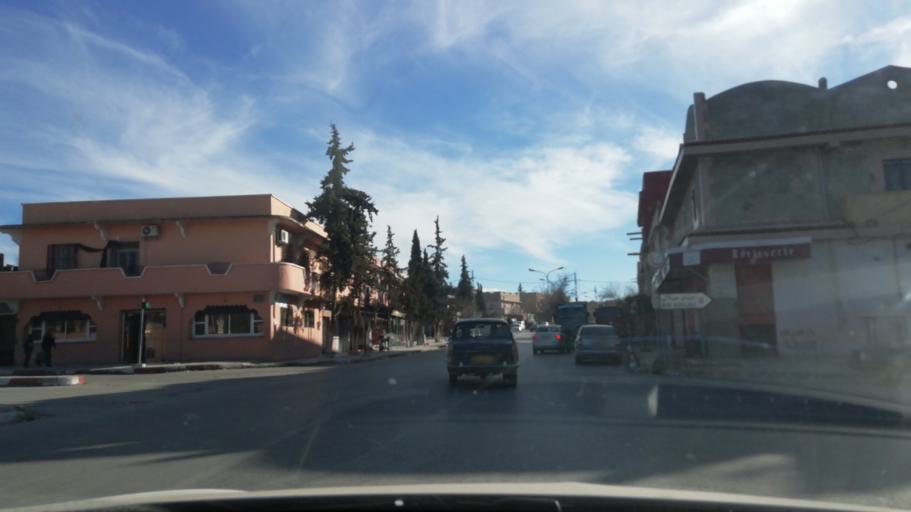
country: DZ
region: Tlemcen
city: Sebdou
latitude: 34.6337
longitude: -1.3332
